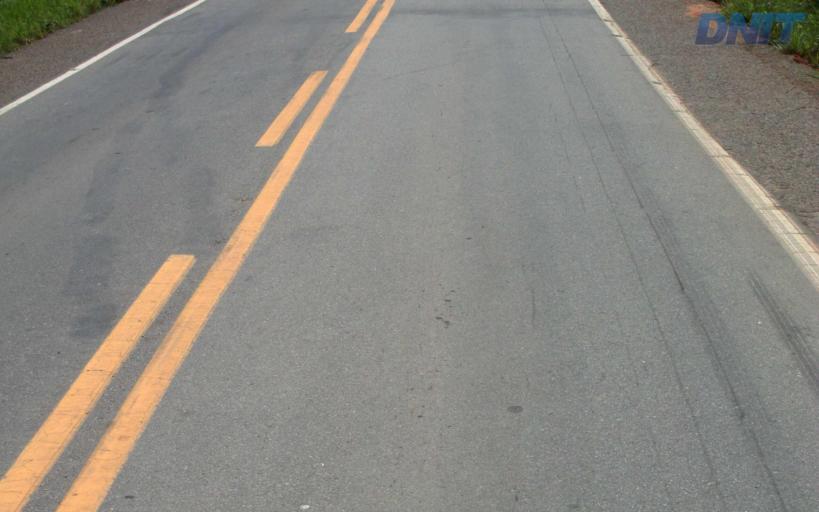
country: BR
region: Minas Gerais
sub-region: Governador Valadares
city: Governador Valadares
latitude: -19.0605
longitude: -42.1614
